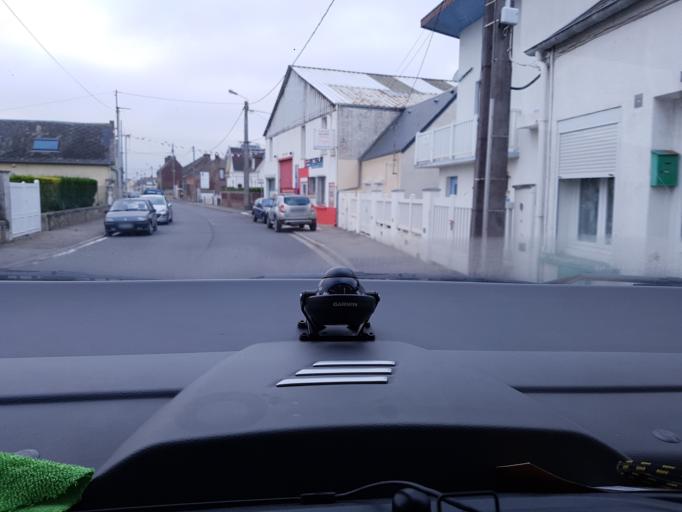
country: FR
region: Picardie
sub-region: Departement de la Somme
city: Cayeux-sur-Mer
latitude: 50.1781
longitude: 1.4932
